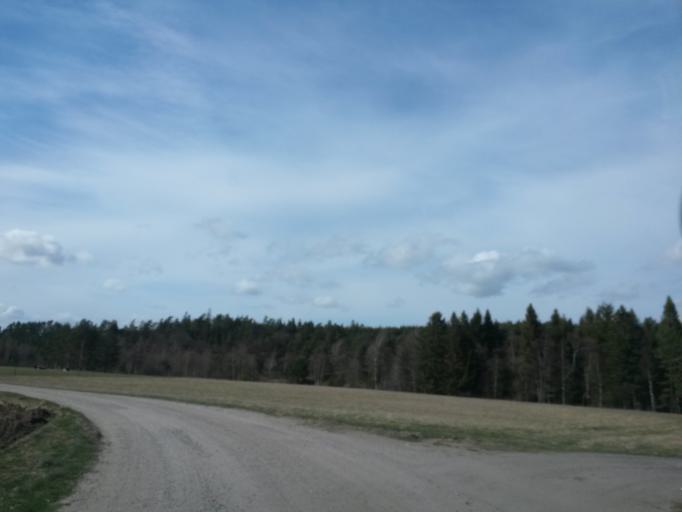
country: SE
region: Vaestra Goetaland
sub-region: Vargarda Kommun
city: Jonstorp
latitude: 57.9446
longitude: 12.6969
